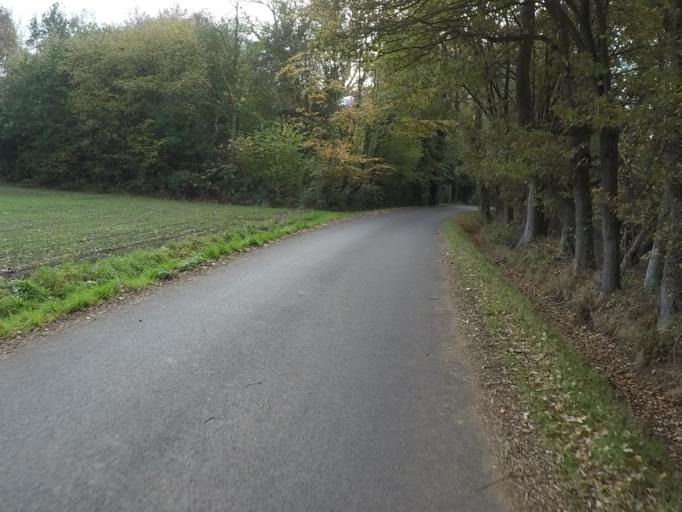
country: BE
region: Flanders
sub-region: Provincie Antwerpen
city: Nijlen
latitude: 51.1444
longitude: 4.6571
